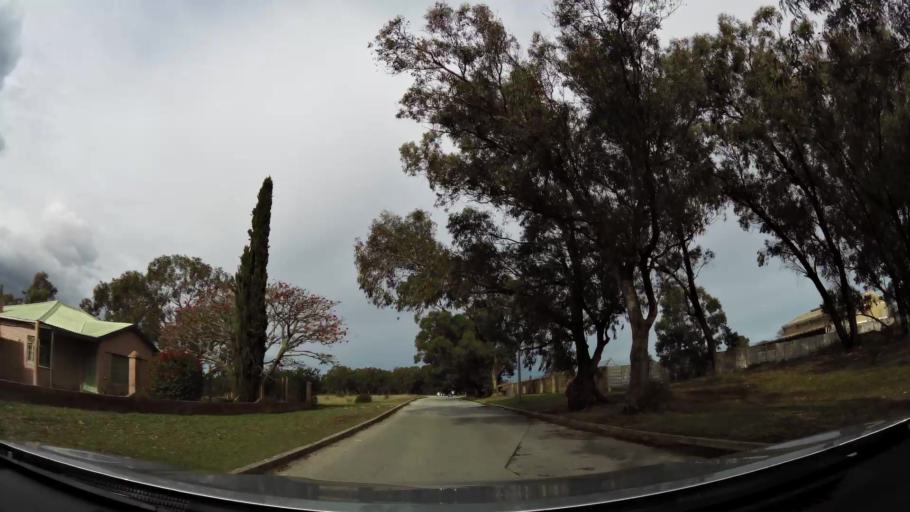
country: ZA
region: Eastern Cape
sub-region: Nelson Mandela Bay Metropolitan Municipality
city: Port Elizabeth
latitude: -33.9358
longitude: 25.4922
